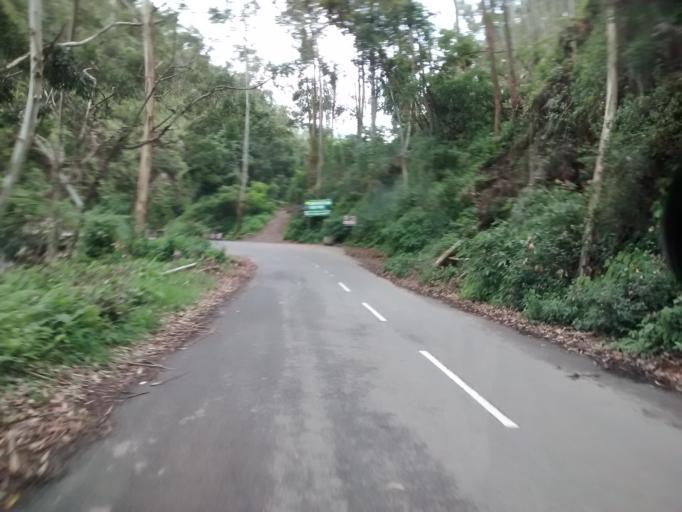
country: IN
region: Kerala
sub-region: Idukki
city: Munnar
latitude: 10.1167
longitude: 77.1499
